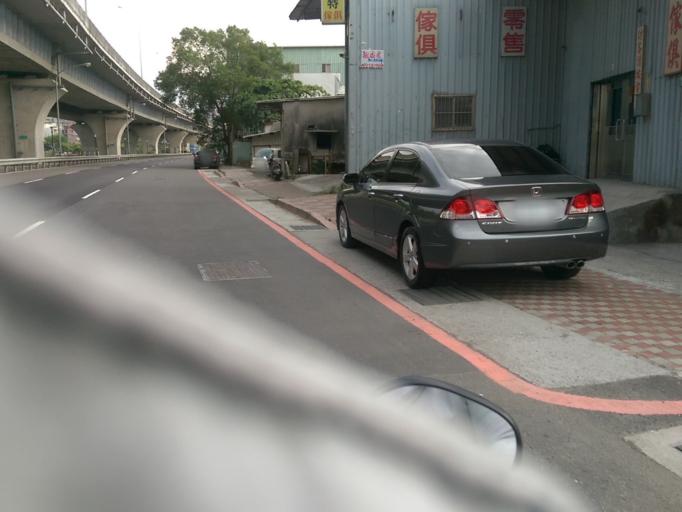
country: TW
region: Taipei
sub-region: Taipei
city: Banqiao
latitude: 25.0137
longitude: 121.4501
